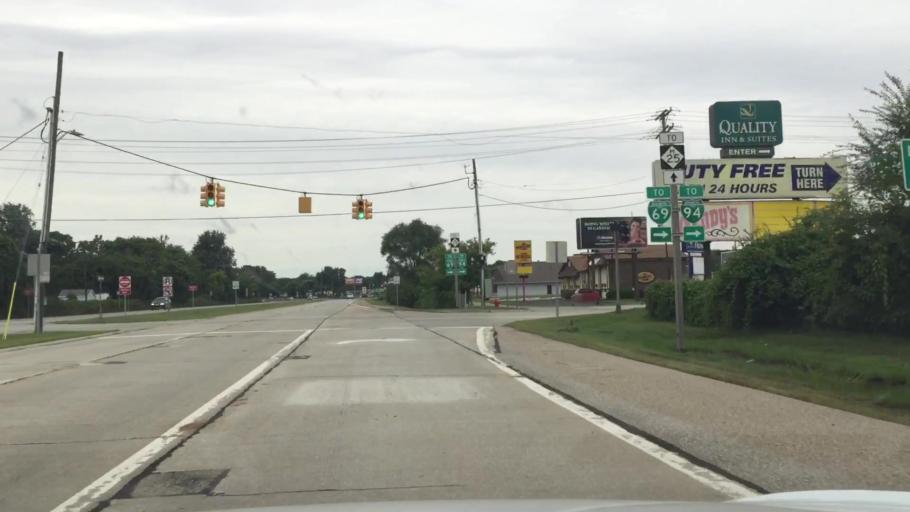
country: US
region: Michigan
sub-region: Saint Clair County
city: Port Huron
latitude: 43.0010
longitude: -82.4413
